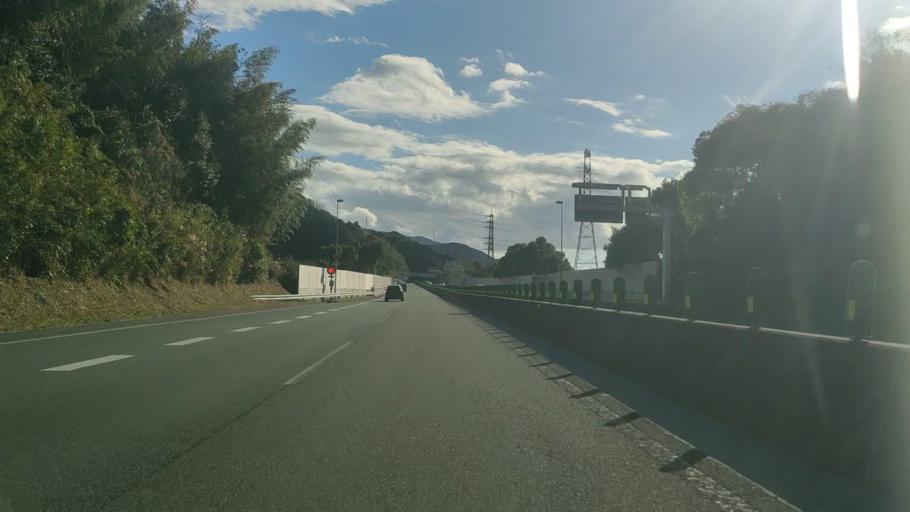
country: JP
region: Fukuoka
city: Kitakyushu
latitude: 33.8384
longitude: 130.7654
